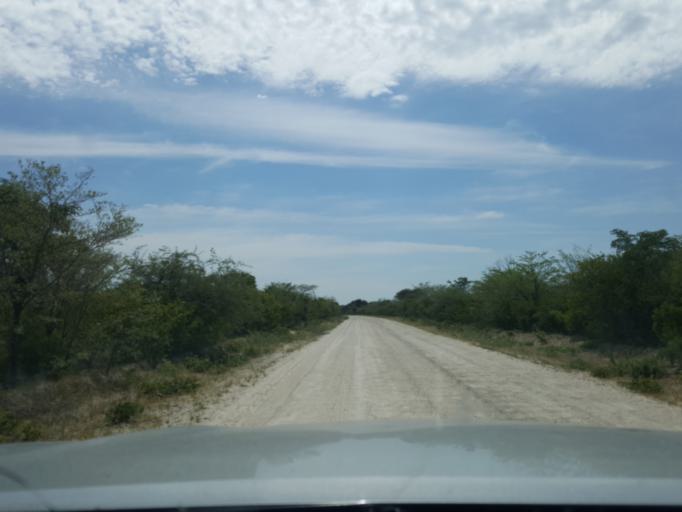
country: BW
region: North West
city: Shakawe
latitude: -18.6470
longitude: 21.9393
